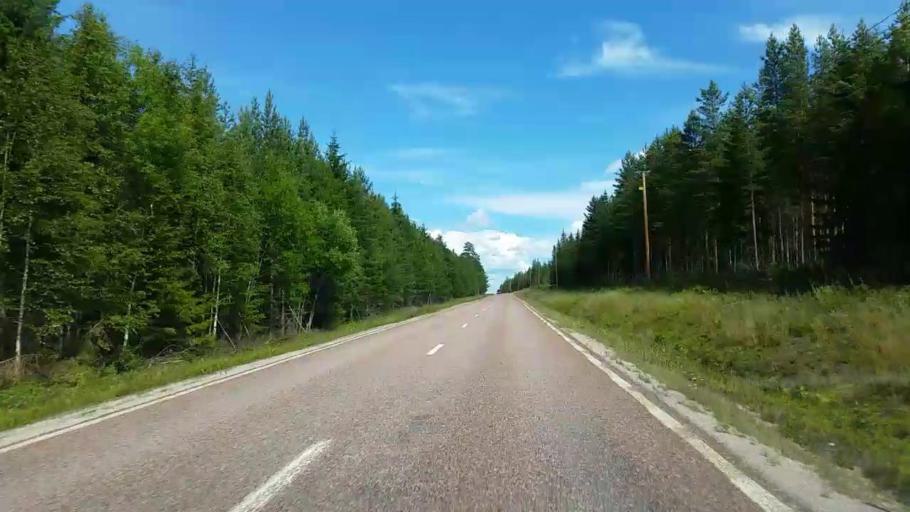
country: SE
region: Dalarna
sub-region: Rattviks Kommun
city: Raettvik
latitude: 61.2002
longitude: 15.3471
